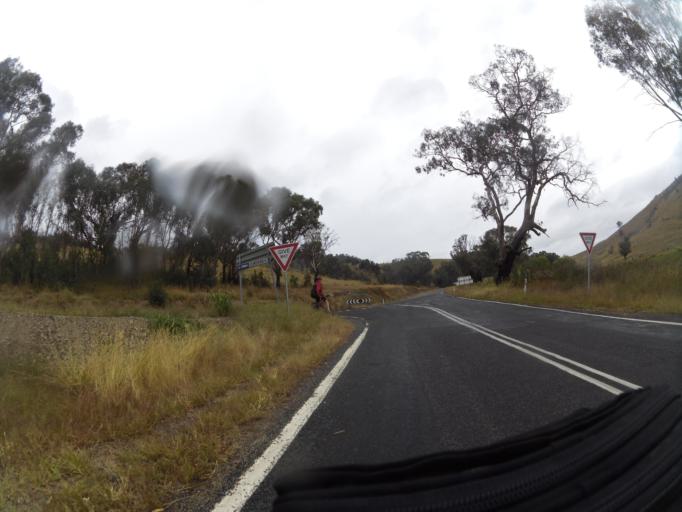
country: AU
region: New South Wales
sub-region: Greater Hume Shire
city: Holbrook
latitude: -36.2212
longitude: 147.7295
